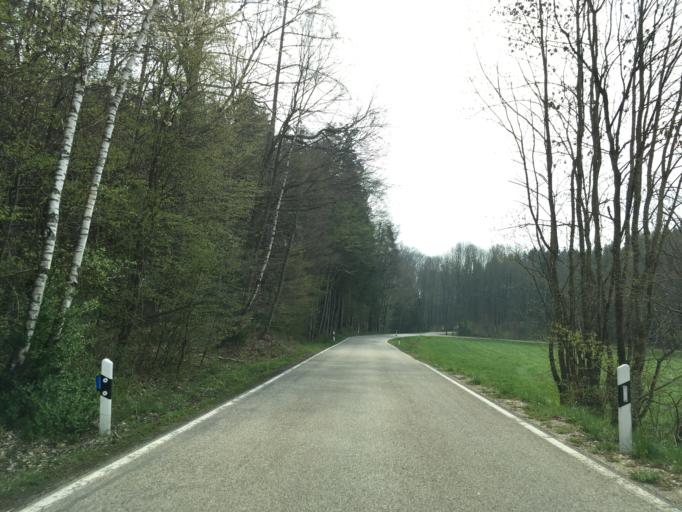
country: DE
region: Bavaria
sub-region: Upper Bavaria
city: Jettenbach
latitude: 48.1554
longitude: 12.3810
